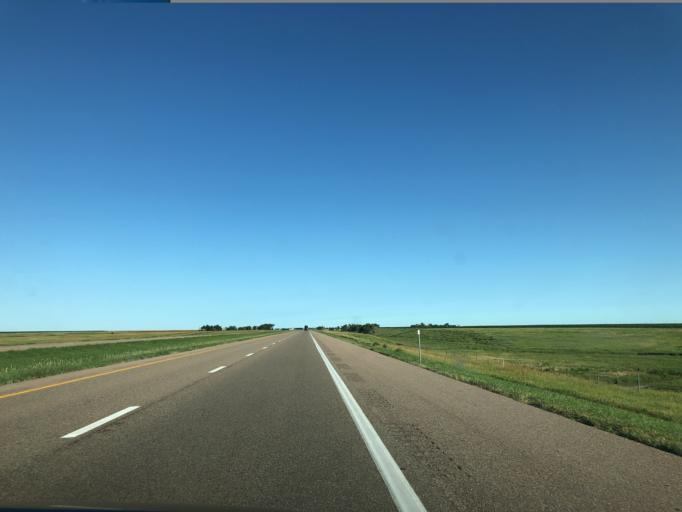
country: US
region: Kansas
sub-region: Gove County
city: Gove
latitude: 39.0870
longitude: -100.3032
